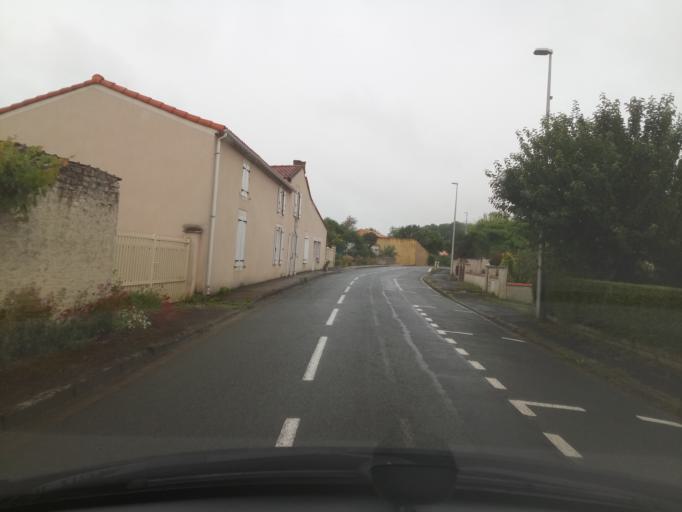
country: FR
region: Poitou-Charentes
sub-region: Departement de la Charente-Maritime
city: Verines
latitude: 46.2280
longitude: -0.9900
